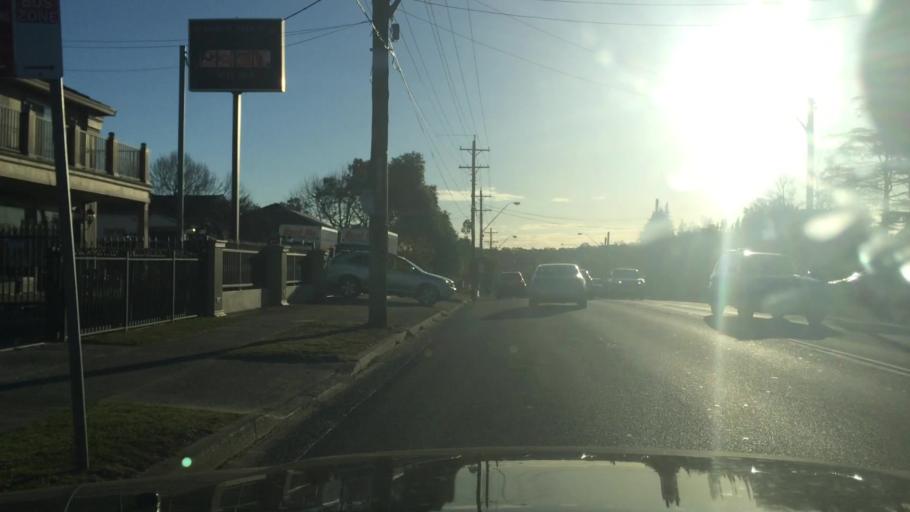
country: AU
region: New South Wales
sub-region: Fairfield
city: Fairfield Heights
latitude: -33.8508
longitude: 150.9218
